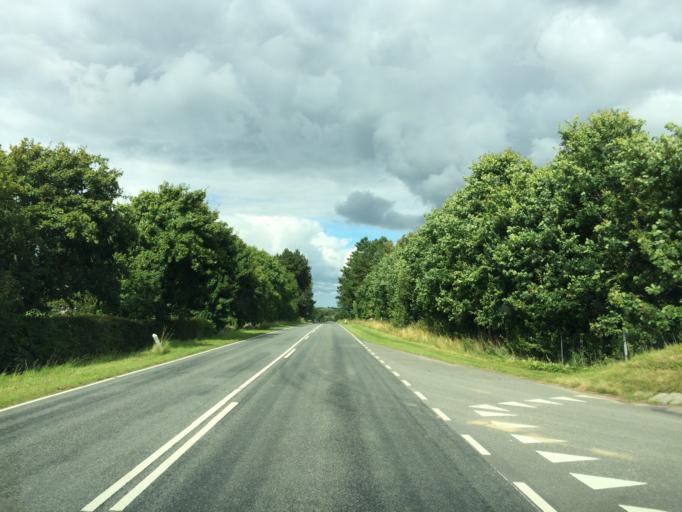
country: DK
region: South Denmark
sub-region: Assens Kommune
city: Harby
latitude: 55.2201
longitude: 10.1686
